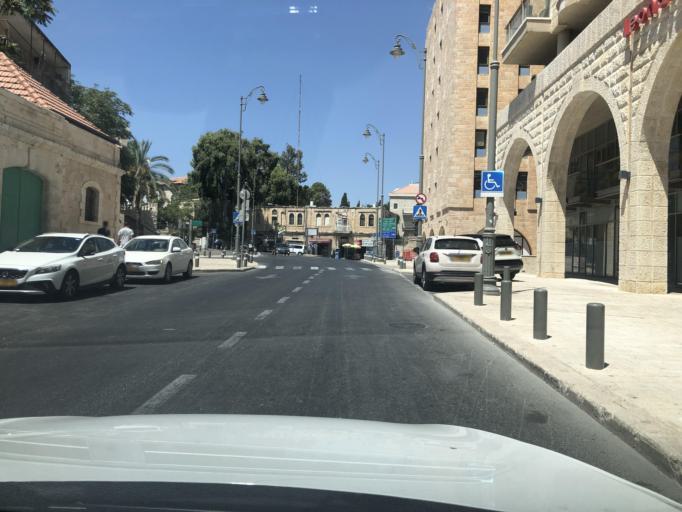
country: IL
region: Jerusalem
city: West Jerusalem
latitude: 31.7829
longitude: 35.2223
